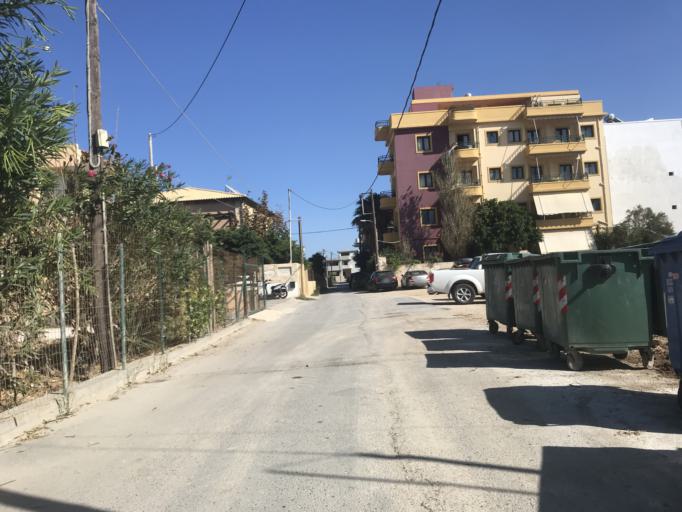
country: GR
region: Crete
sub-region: Nomos Irakleiou
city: Gazi
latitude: 35.3378
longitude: 25.0682
